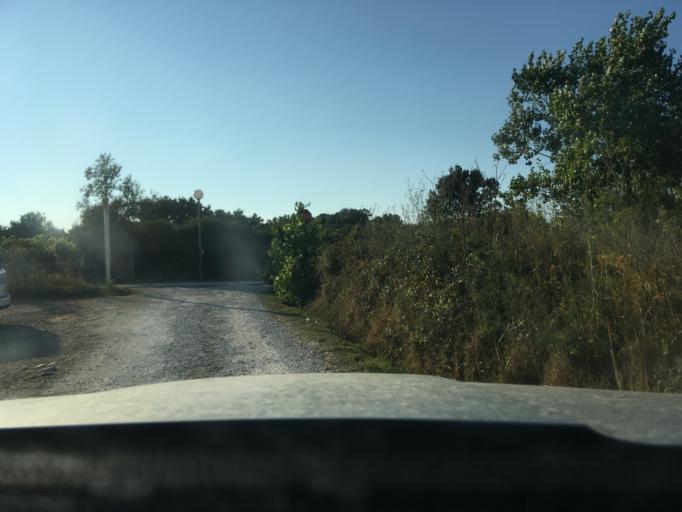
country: HR
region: Zadarska
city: Vir
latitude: 44.2945
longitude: 15.0738
